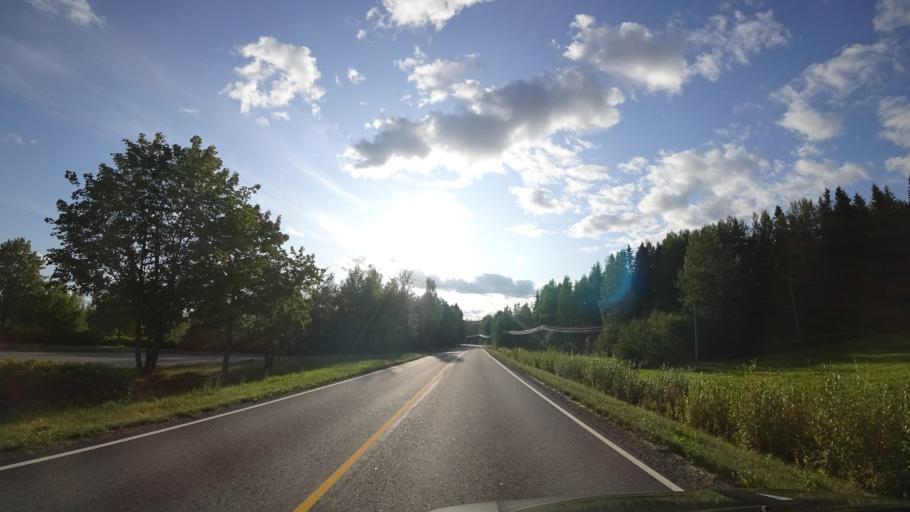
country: FI
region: Paijanne Tavastia
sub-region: Lahti
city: Haemeenkoski
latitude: 61.0820
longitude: 25.1333
